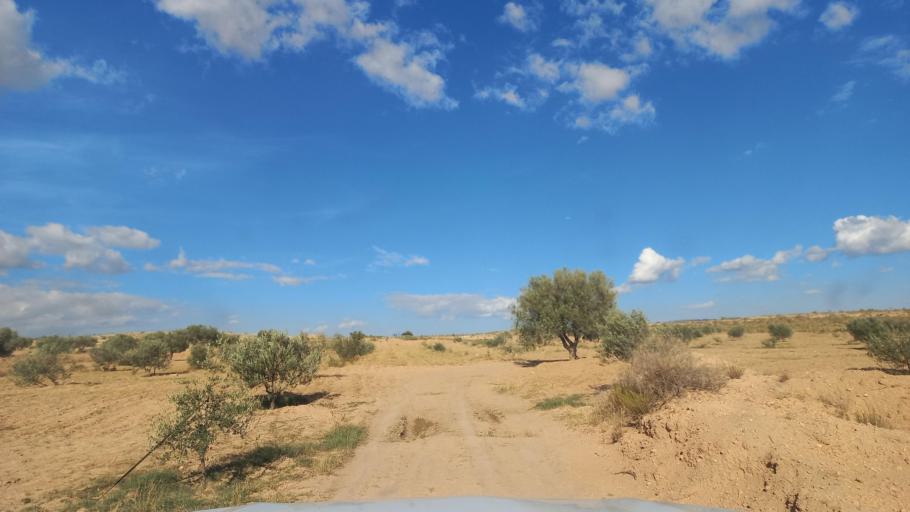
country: TN
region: Al Qasrayn
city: Sbiba
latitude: 35.3977
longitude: 9.0123
